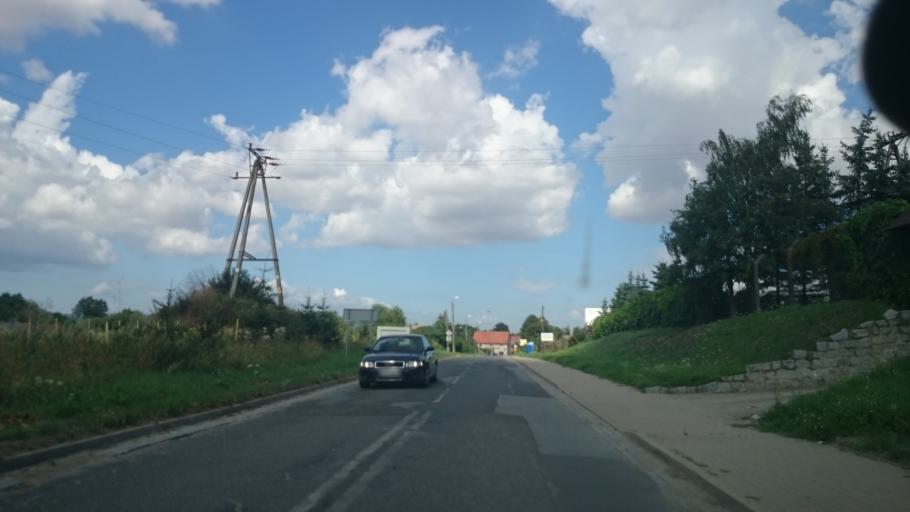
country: PL
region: Lower Silesian Voivodeship
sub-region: Powiat zabkowicki
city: Zabkowice Slaskie
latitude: 50.5790
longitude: 16.8305
